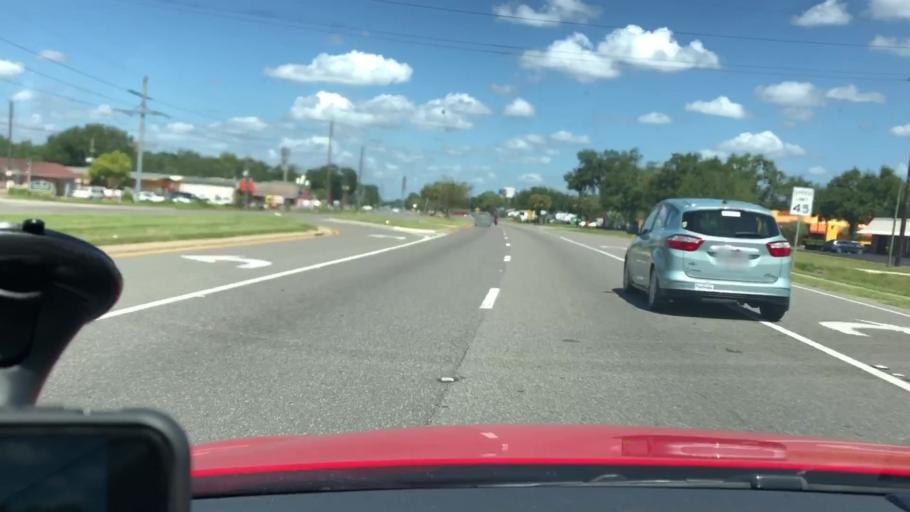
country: US
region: Florida
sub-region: Volusia County
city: Orange City
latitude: 28.9245
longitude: -81.2990
